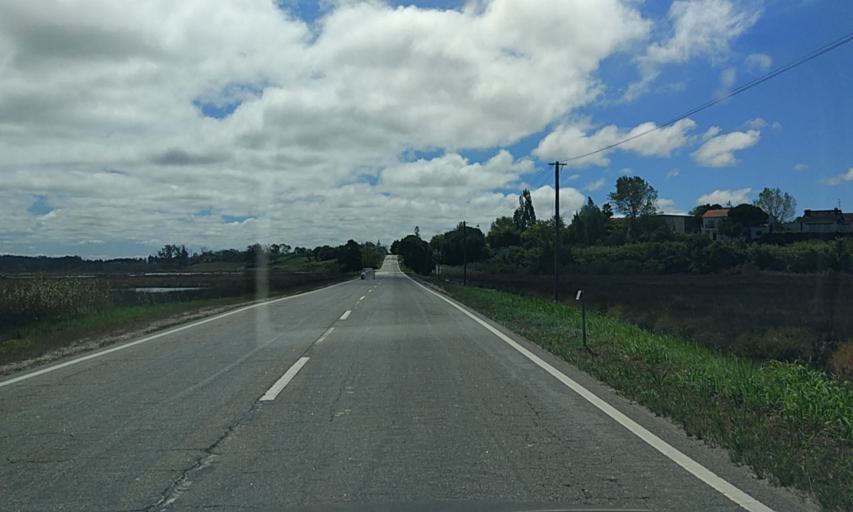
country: PT
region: Aveiro
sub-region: Vagos
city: Vagos
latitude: 40.5700
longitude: -8.6819
